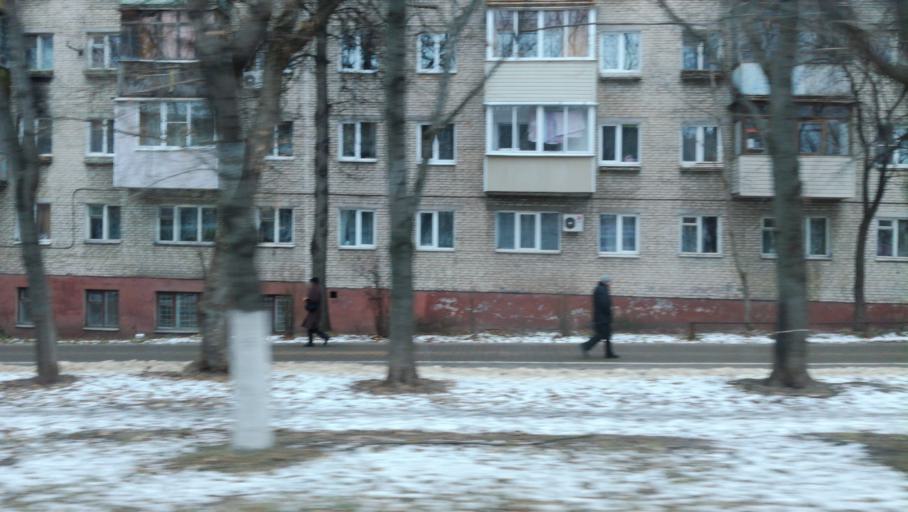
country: RU
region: Tula
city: Tula
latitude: 54.1900
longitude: 37.5924
